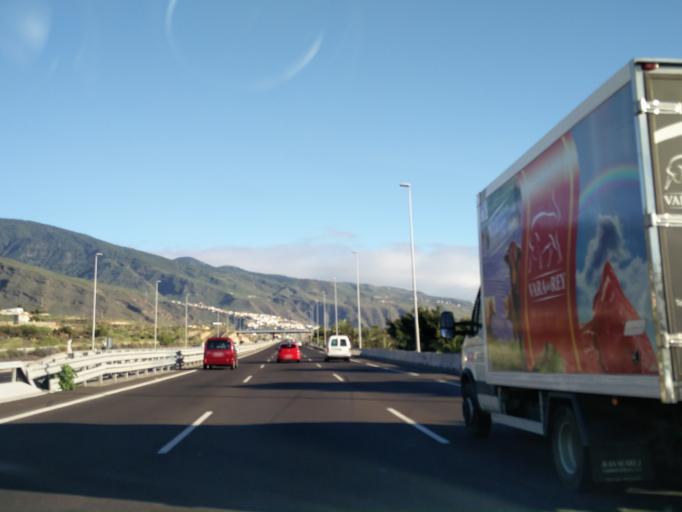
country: ES
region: Canary Islands
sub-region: Provincia de Santa Cruz de Tenerife
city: Candelaria
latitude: 28.3383
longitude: -16.3740
